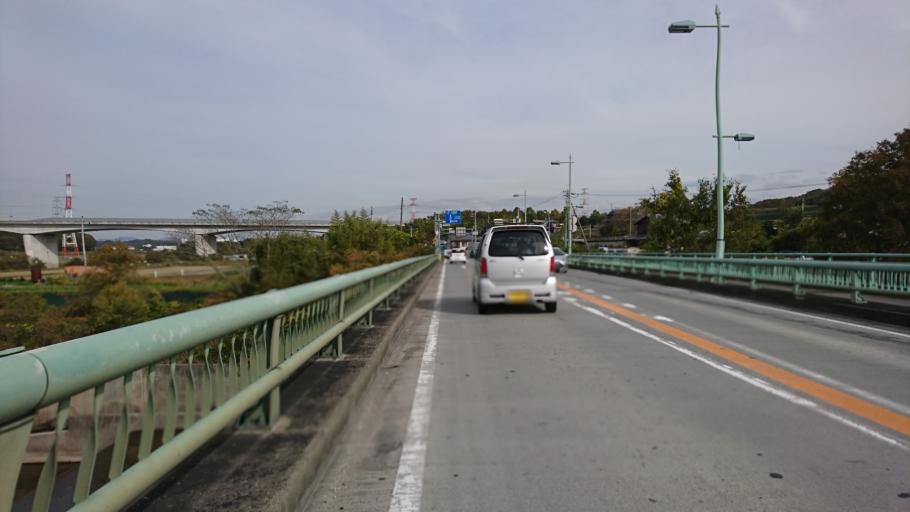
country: JP
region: Hyogo
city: Ono
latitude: 34.8086
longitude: 134.9290
